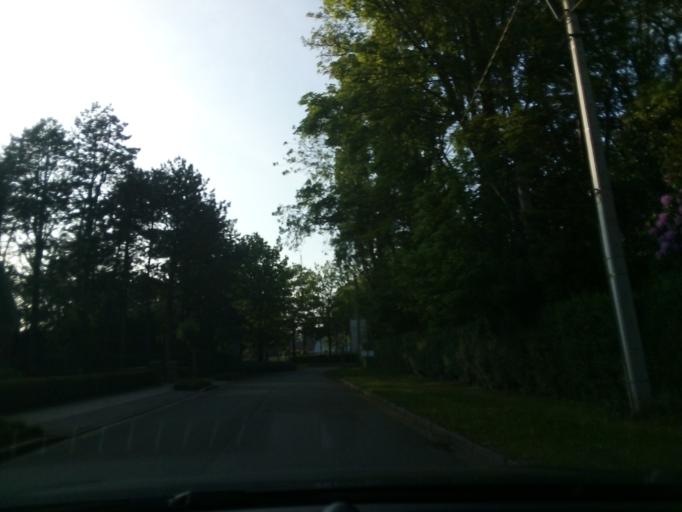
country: BE
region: Flanders
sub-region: Provincie West-Vlaanderen
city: Roeselare
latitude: 50.9377
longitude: 3.1487
